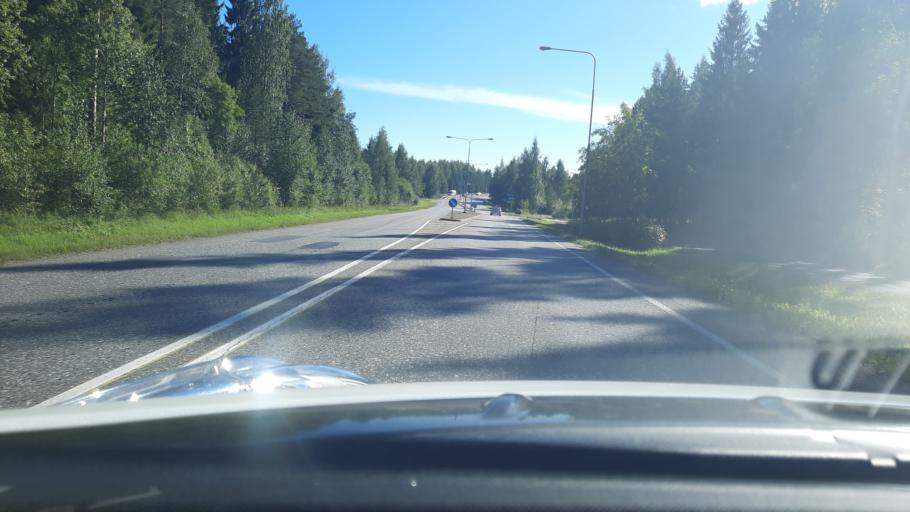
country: FI
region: North Karelia
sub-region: Joensuu
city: Joensuu
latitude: 62.6333
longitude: 29.7006
